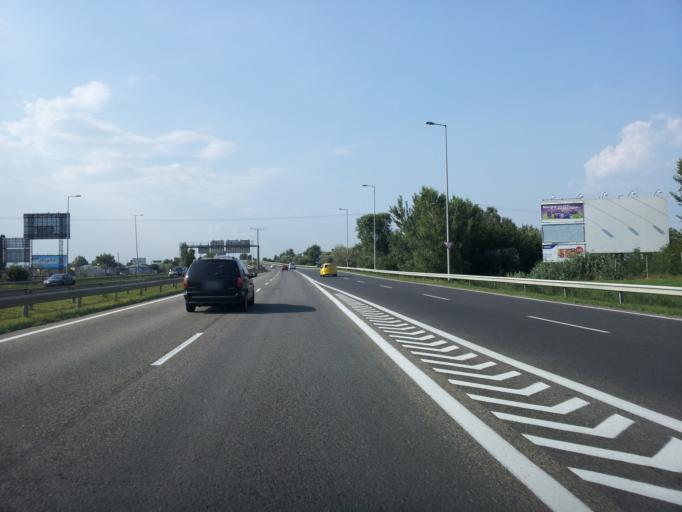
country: HU
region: Budapest
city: Budapest XIX. keruelet
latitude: 47.4285
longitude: 19.1505
